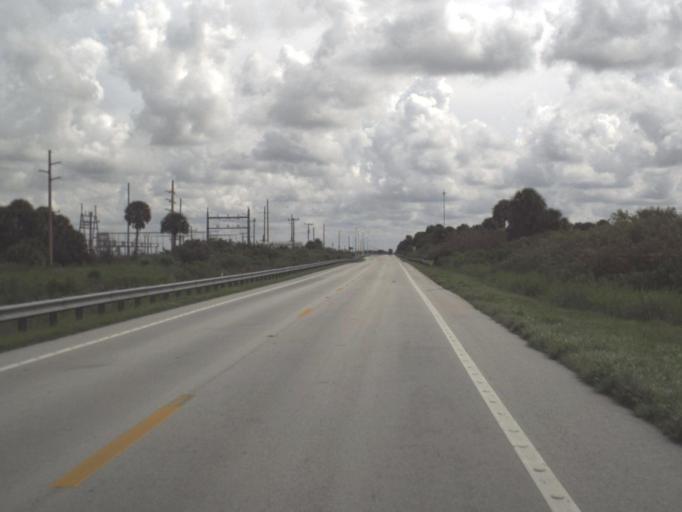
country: US
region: Florida
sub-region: Glades County
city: Buckhead Ridge
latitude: 27.2361
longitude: -81.0728
